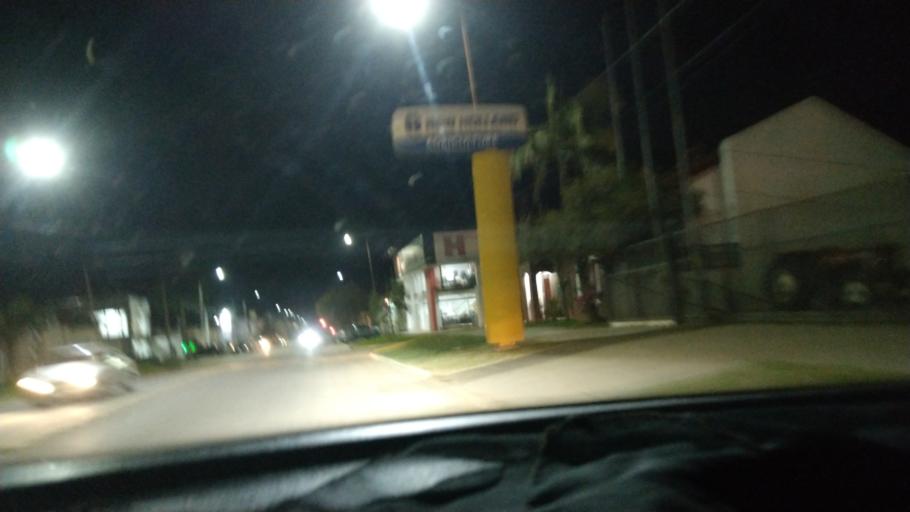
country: AR
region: Entre Rios
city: Chajari
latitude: -30.7638
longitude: -57.9936
